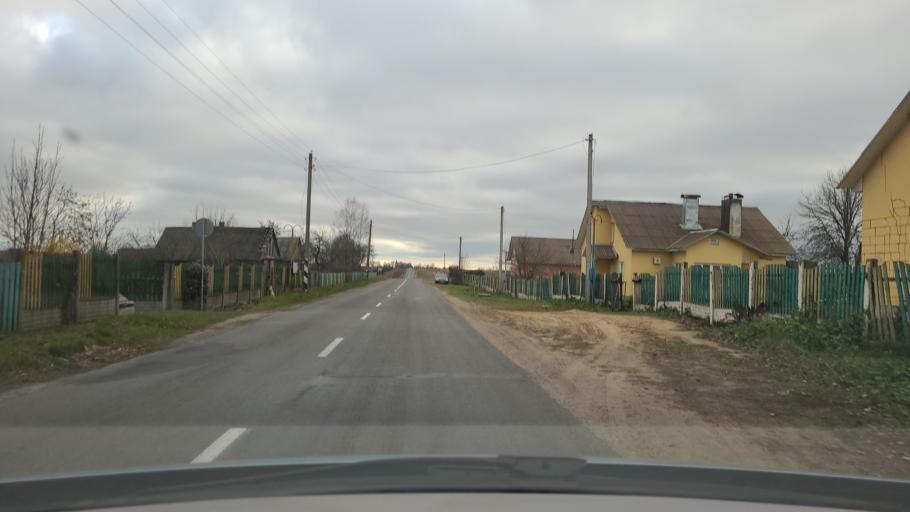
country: BY
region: Minsk
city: Khalopyenichy
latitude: 54.4529
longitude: 28.9859
